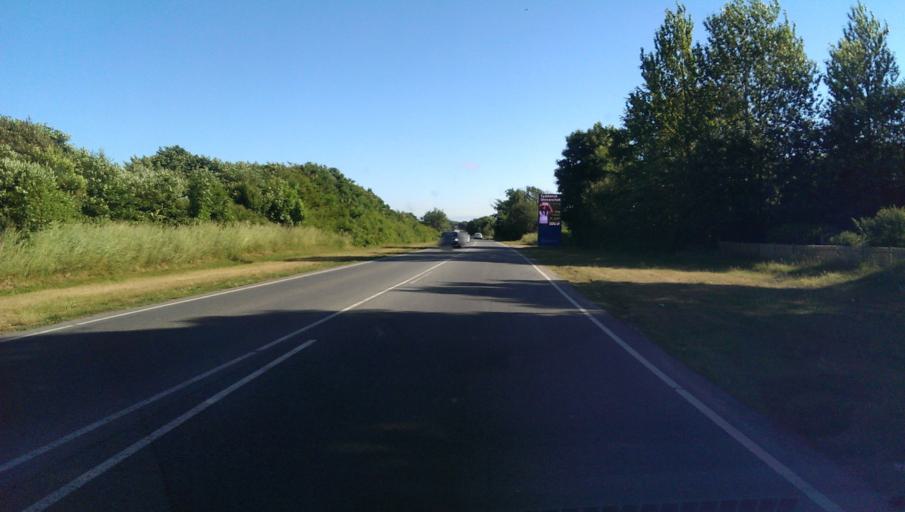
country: DK
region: South Denmark
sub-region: Esbjerg Kommune
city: Esbjerg
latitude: 55.5171
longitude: 8.4064
